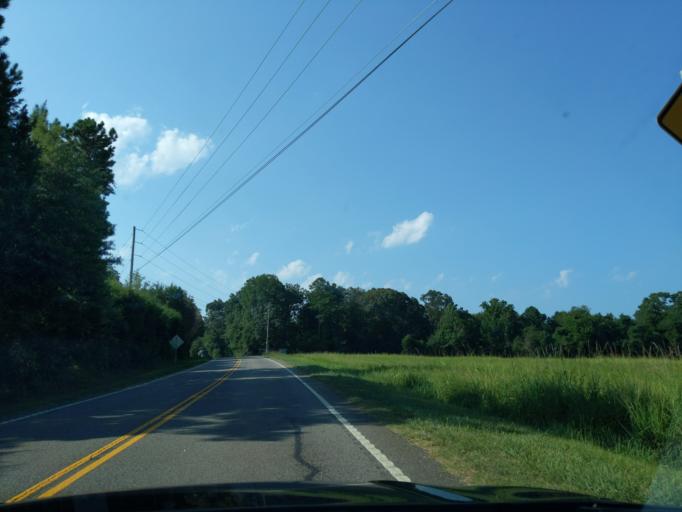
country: US
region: South Carolina
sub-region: Newberry County
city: Prosperity
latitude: 34.0632
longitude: -81.5610
